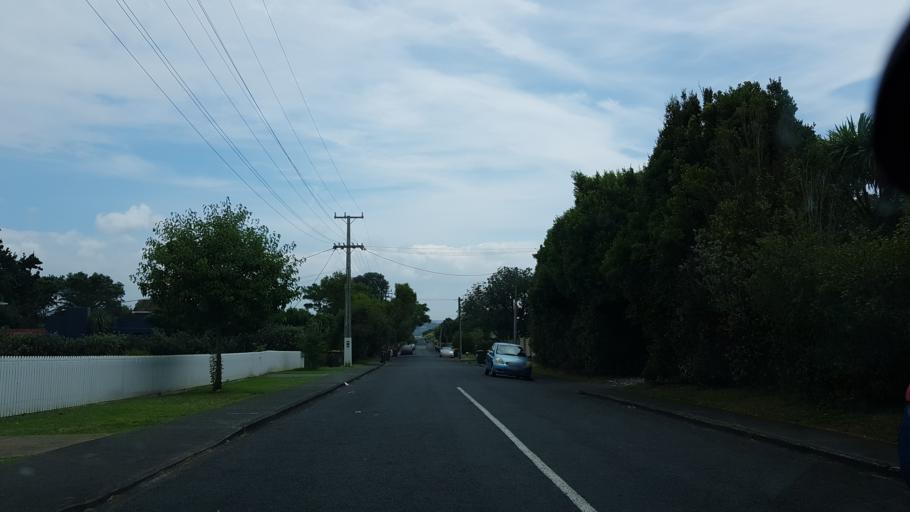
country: NZ
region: Auckland
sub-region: Auckland
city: North Shore
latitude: -36.8022
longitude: 174.7749
